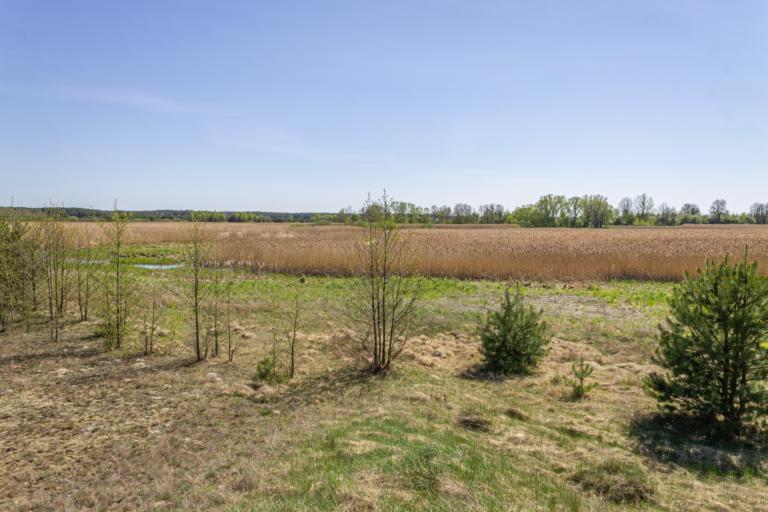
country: BY
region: Brest
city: Kamyanyets
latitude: 52.4451
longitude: 23.9015
